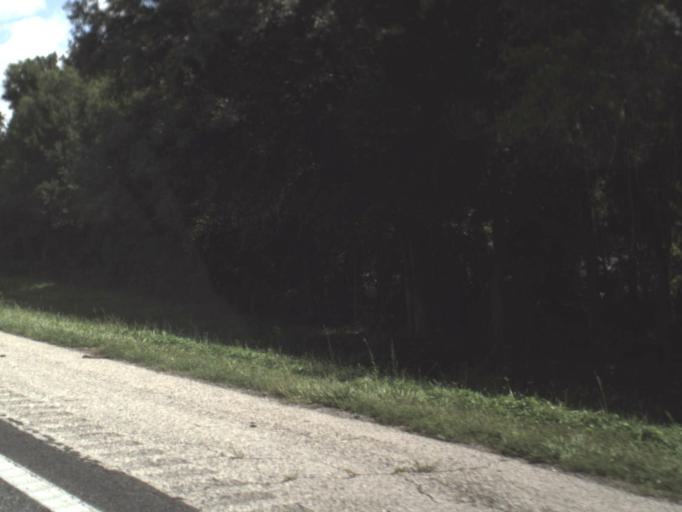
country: US
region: Florida
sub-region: Alachua County
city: Alachua
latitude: 29.7808
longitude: -82.5117
